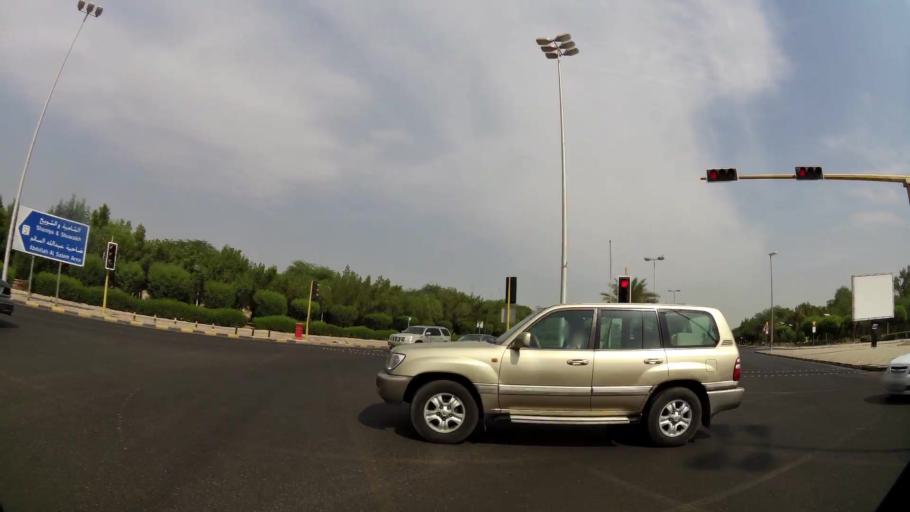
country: KW
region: Al Asimah
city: Ash Shamiyah
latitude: 29.3456
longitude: 47.9830
